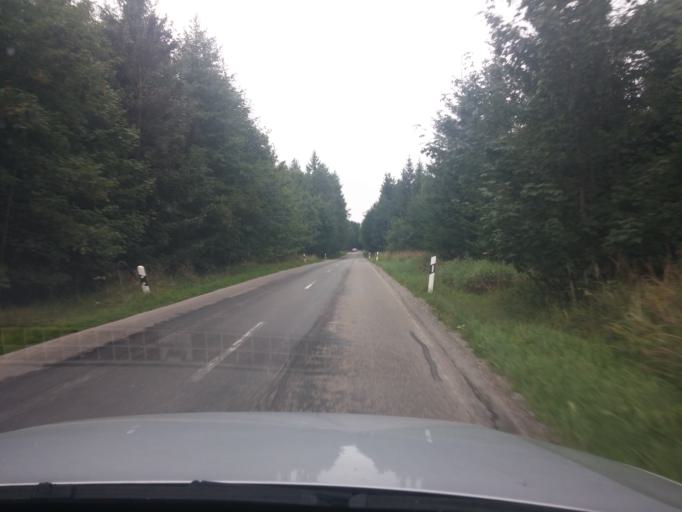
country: DE
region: Bavaria
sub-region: Swabia
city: Kronburg
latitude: 47.9248
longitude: 10.1540
